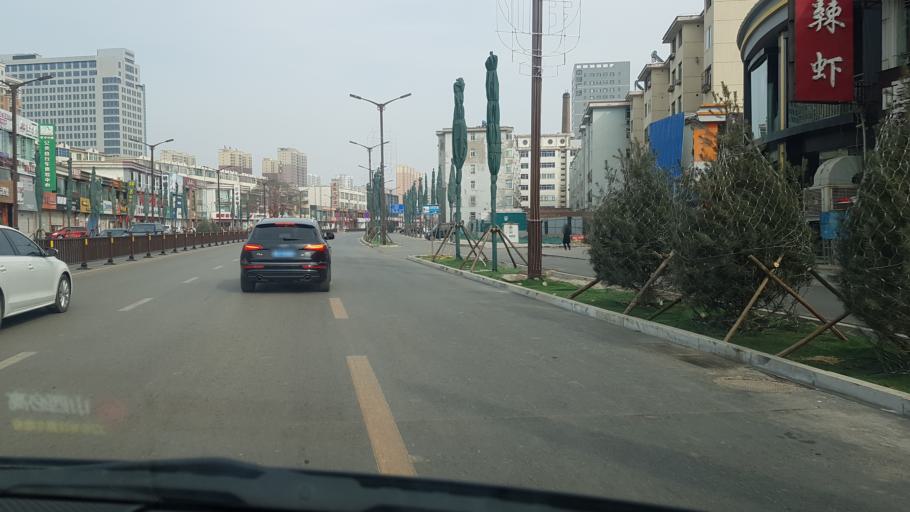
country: CN
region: Shanxi Sheng
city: Yuci
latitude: 37.6919
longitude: 112.7366
